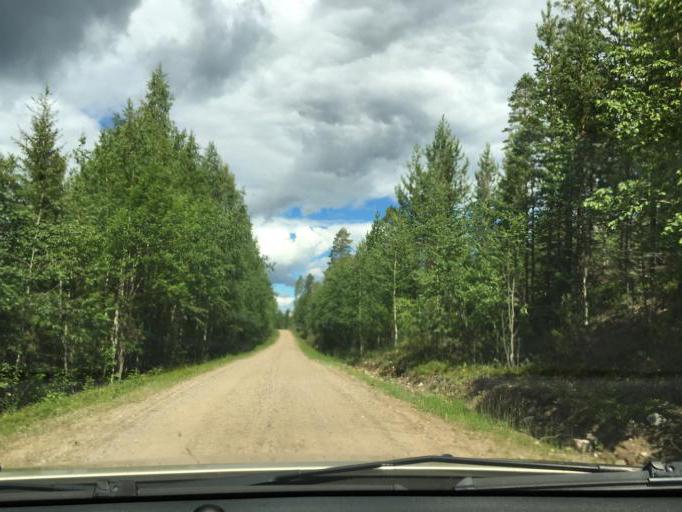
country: SE
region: Norrbotten
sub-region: Overkalix Kommun
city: OEverkalix
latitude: 66.1590
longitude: 22.8561
